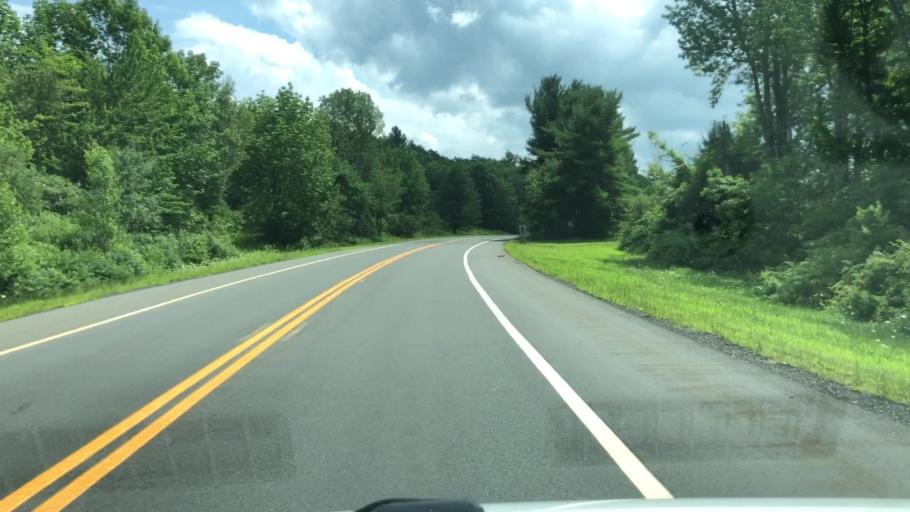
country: US
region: Massachusetts
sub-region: Franklin County
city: Ashfield
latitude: 42.5015
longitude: -72.8097
